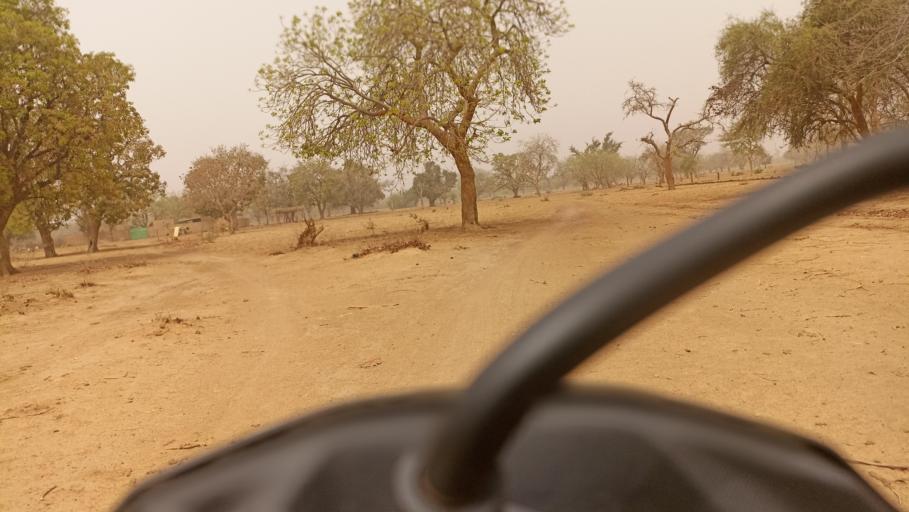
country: BF
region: Nord
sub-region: Province du Zondoma
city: Gourcy
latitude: 13.2497
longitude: -2.6018
